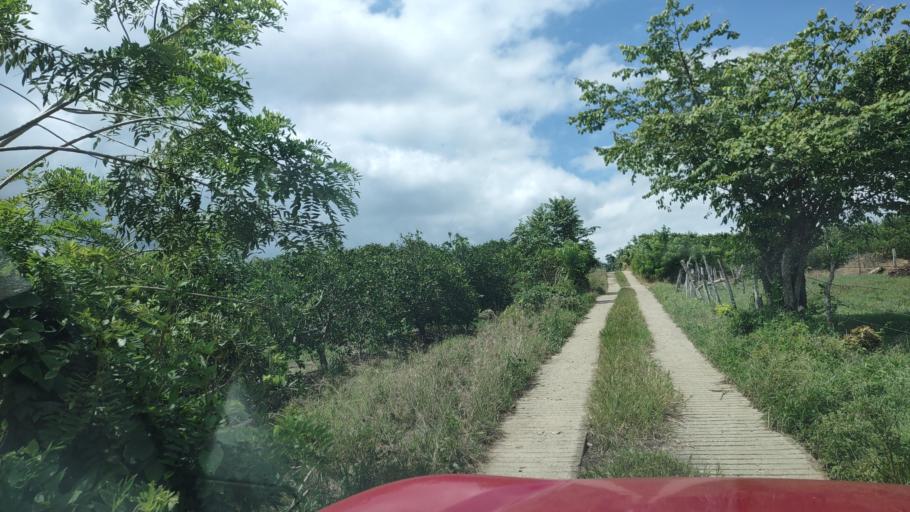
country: MX
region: Puebla
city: San Jose Acateno
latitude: 20.2194
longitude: -97.1407
